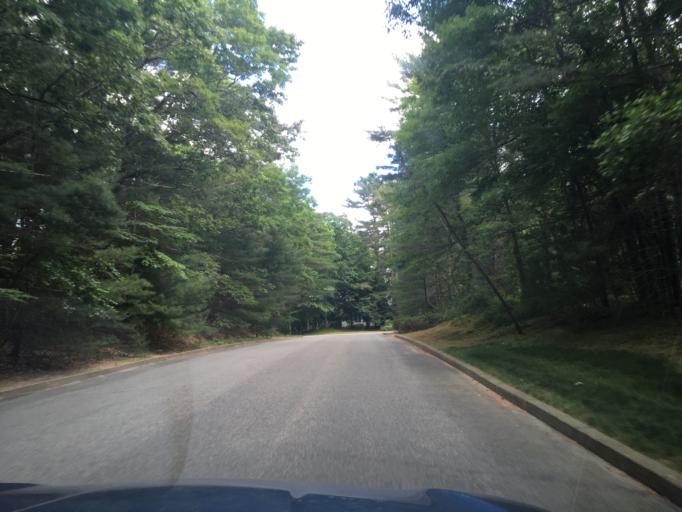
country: US
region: Rhode Island
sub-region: Washington County
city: Exeter
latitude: 41.6295
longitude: -71.5374
